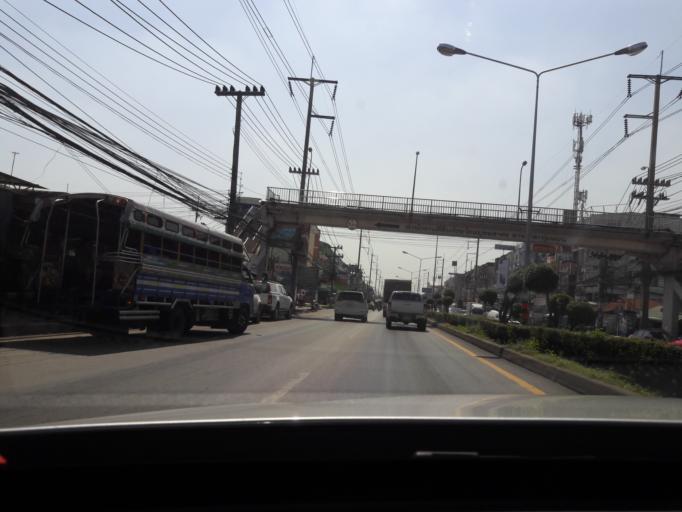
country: TH
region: Samut Sakhon
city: Krathum Baen
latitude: 13.6245
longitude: 100.2928
